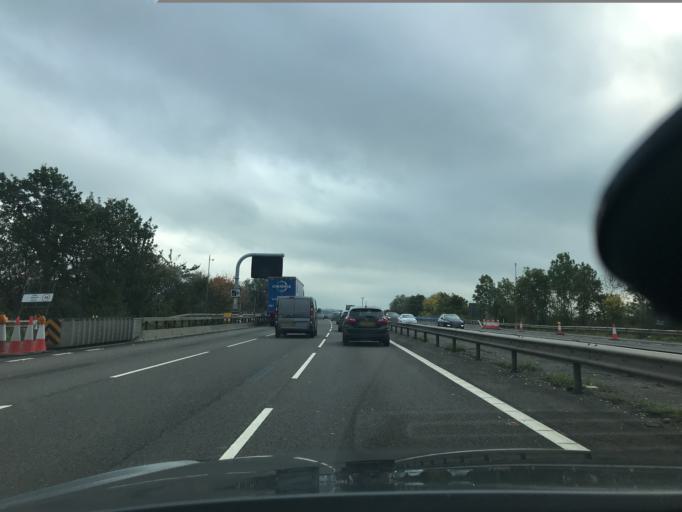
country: GB
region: England
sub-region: Staffordshire
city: Penkridge
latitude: 52.7654
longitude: -2.1100
